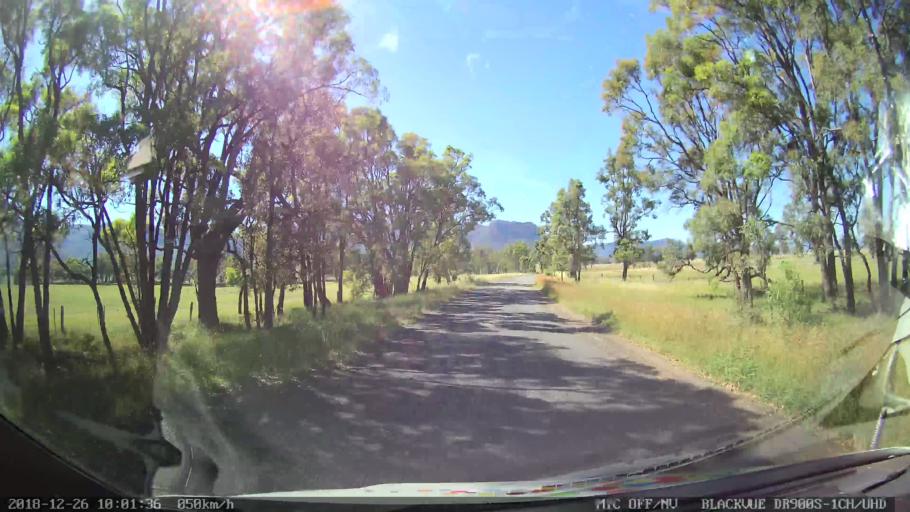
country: AU
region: New South Wales
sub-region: Mid-Western Regional
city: Kandos
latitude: -33.0482
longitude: 150.2222
